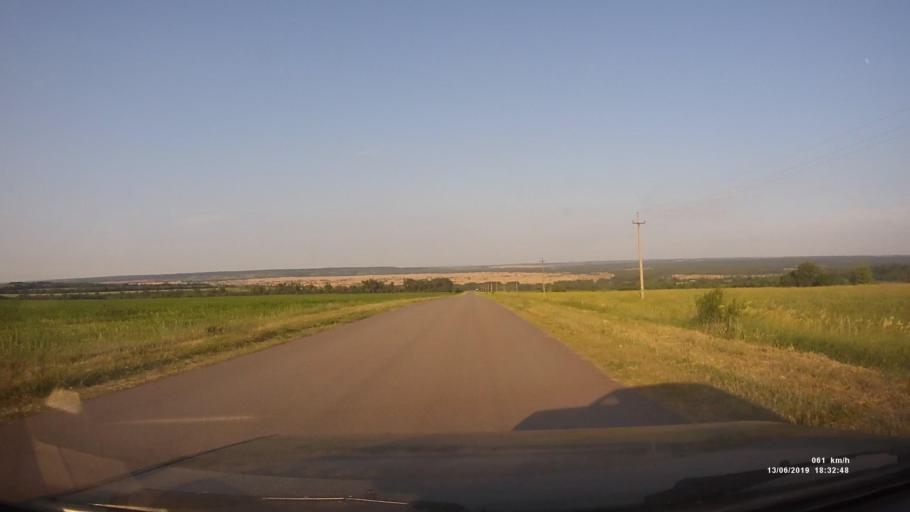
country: RU
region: Rostov
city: Kazanskaya
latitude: 49.8703
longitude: 41.3725
